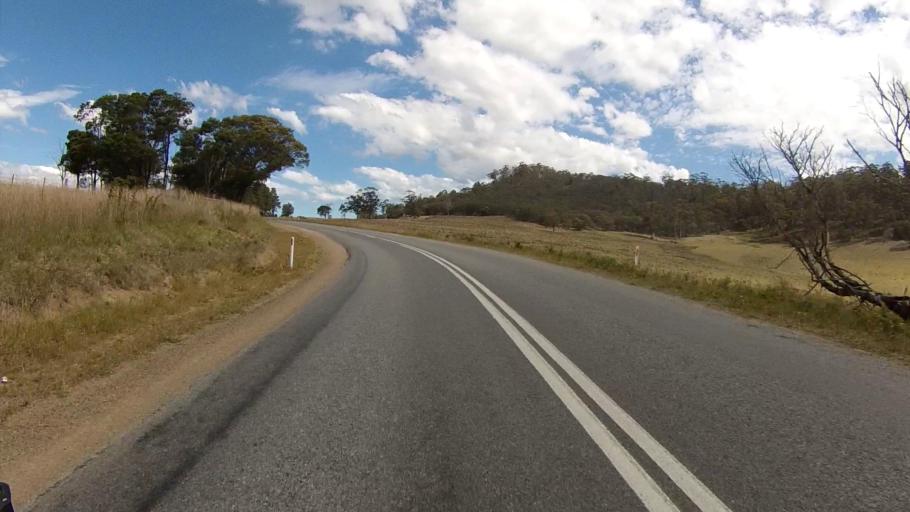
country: AU
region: Tasmania
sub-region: Break O'Day
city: St Helens
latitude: -41.9661
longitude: 148.1520
